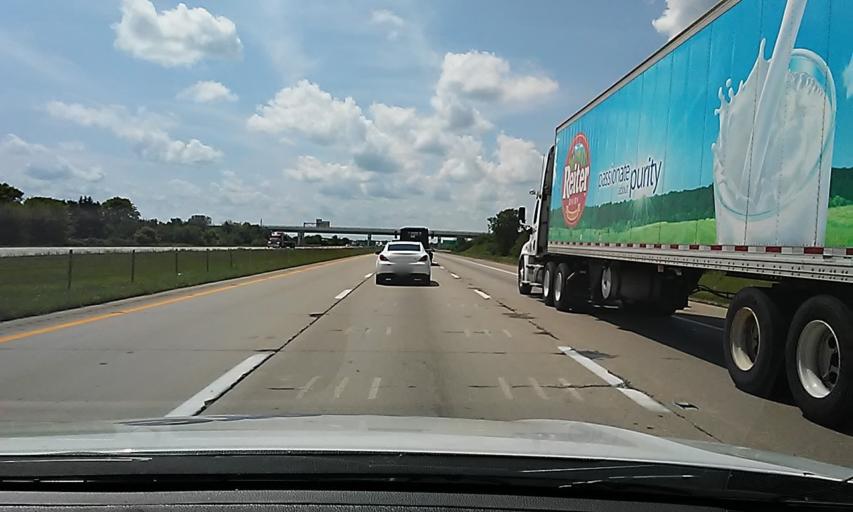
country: US
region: Ohio
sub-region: Madison County
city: West Jefferson
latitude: 39.9730
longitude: -83.2767
